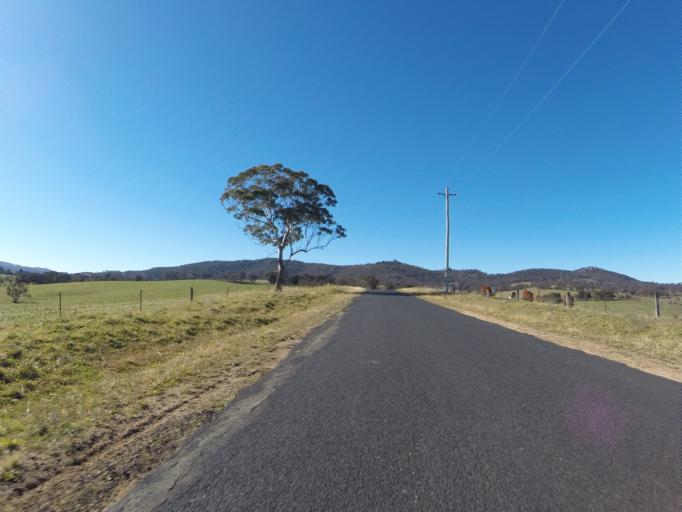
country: AU
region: New South Wales
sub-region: Oberon
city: Oberon
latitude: -33.5359
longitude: 149.8957
